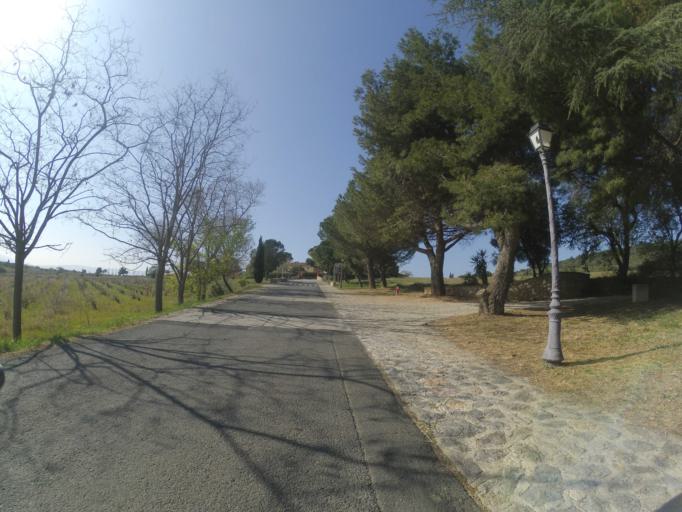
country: FR
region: Languedoc-Roussillon
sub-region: Departement des Pyrenees-Orientales
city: Thuir
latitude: 42.6161
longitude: 2.7484
